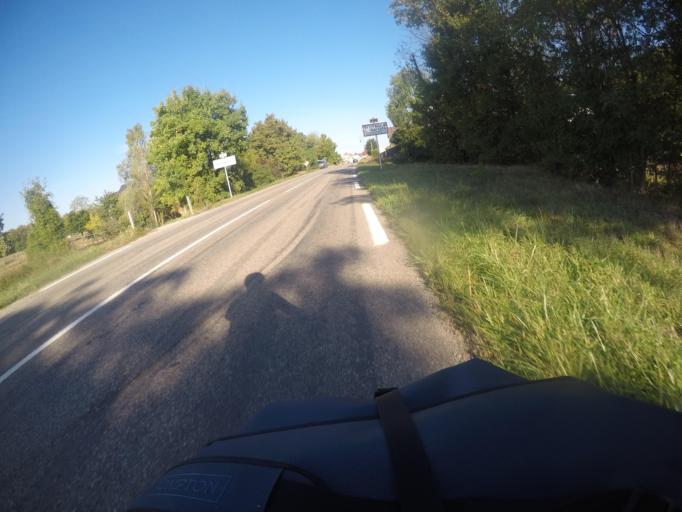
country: FR
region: Alsace
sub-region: Departement du Haut-Rhin
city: Rosenau
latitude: 47.6346
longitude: 7.5196
